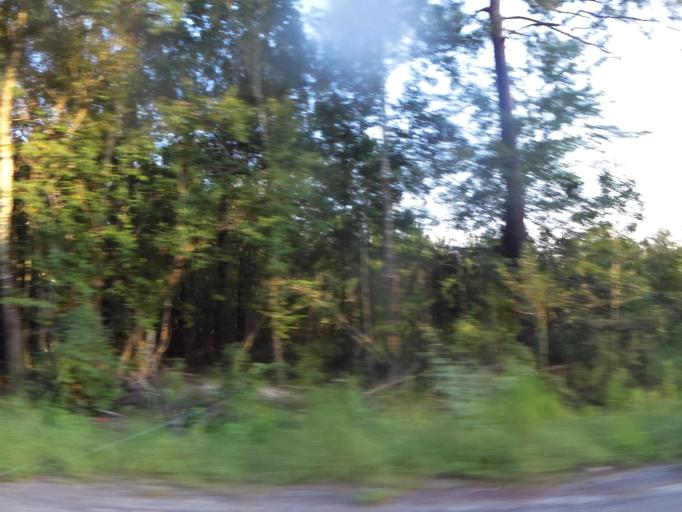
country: US
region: Florida
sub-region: Duval County
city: Baldwin
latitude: 30.3840
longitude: -82.0407
